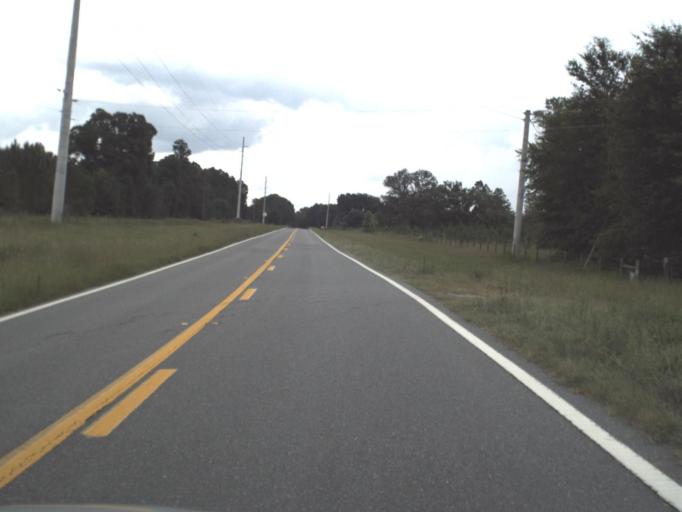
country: US
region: Florida
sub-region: Union County
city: Lake Butler
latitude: 29.9139
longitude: -82.3980
